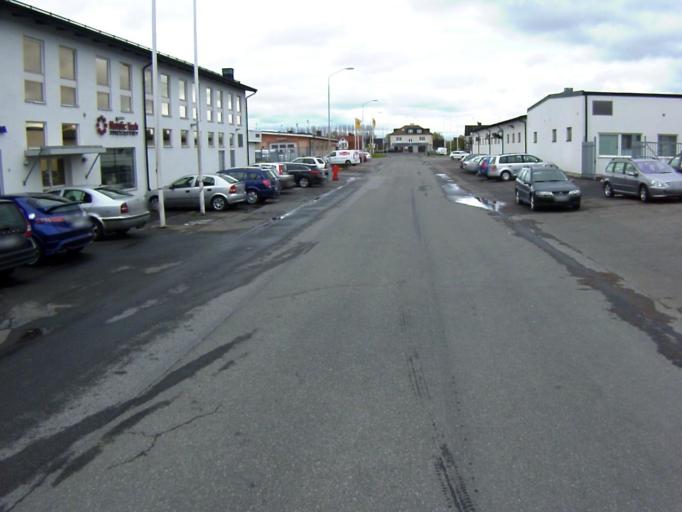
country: SE
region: Skane
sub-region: Kristianstads Kommun
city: Kristianstad
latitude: 56.0221
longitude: 14.1366
